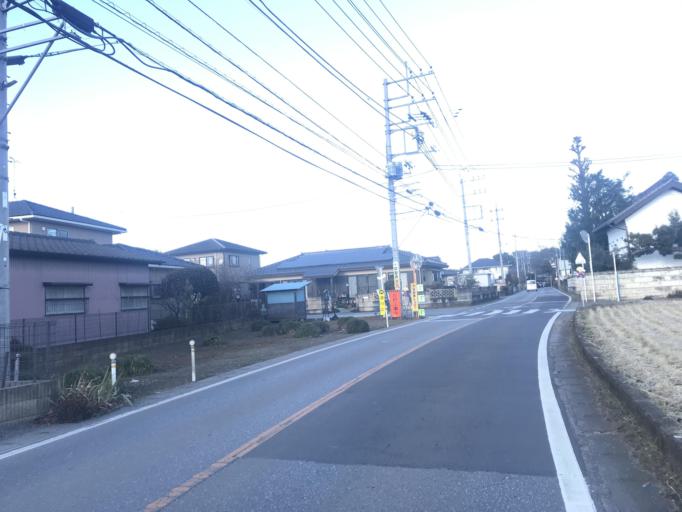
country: JP
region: Tochigi
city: Kaminokawa
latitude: 36.4283
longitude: 139.8703
